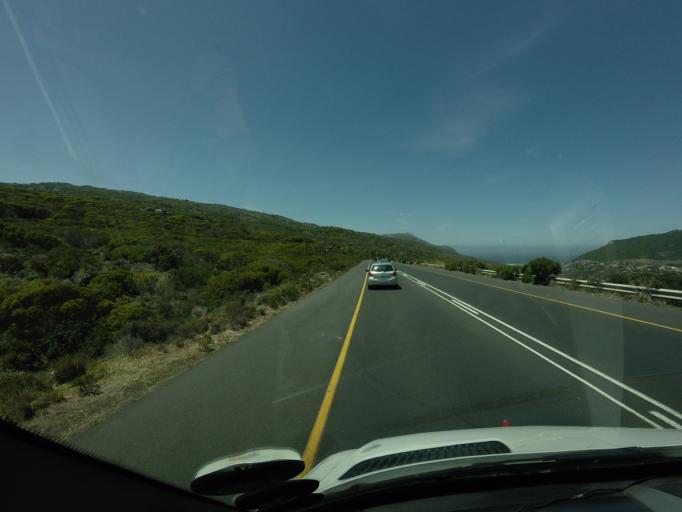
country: ZA
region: Western Cape
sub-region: City of Cape Town
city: Bergvliet
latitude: -34.1459
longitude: 18.4037
